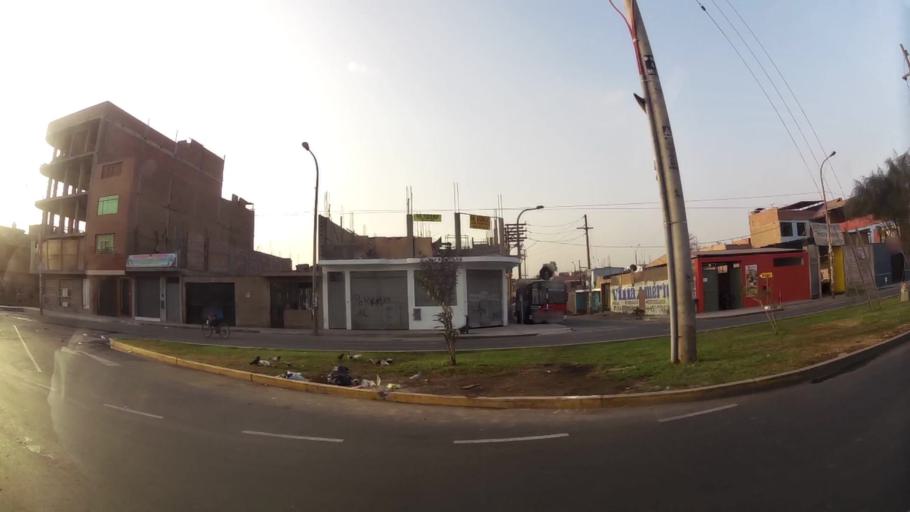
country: PE
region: Lima
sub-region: Lima
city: Independencia
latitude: -11.9897
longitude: -77.0989
